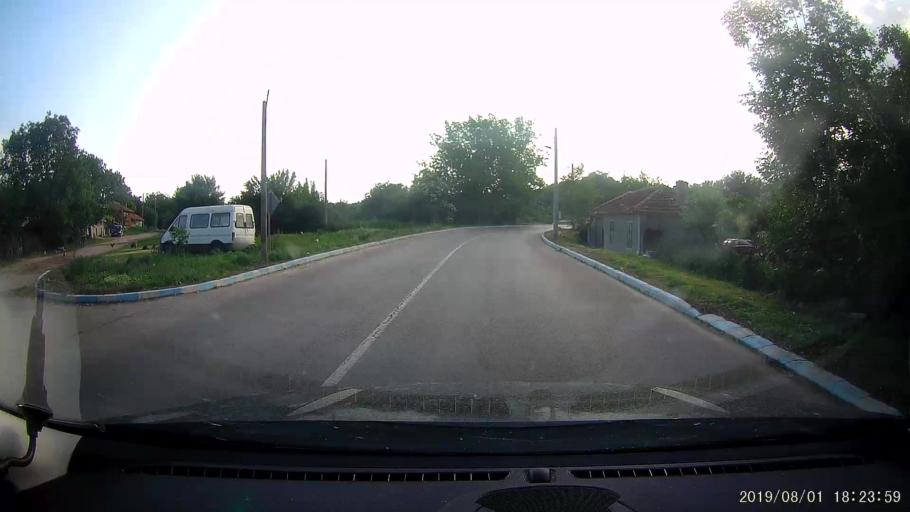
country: BG
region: Shumen
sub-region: Obshtina Kaolinovo
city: Kaolinovo
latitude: 43.6264
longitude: 27.0133
